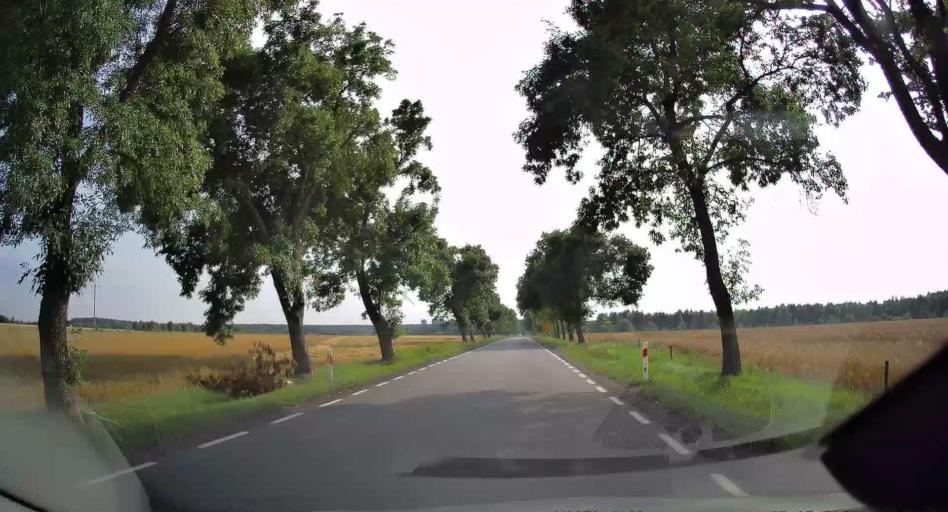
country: PL
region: Lodz Voivodeship
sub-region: Powiat tomaszowski
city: Rzeczyca
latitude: 51.5616
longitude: 20.2649
